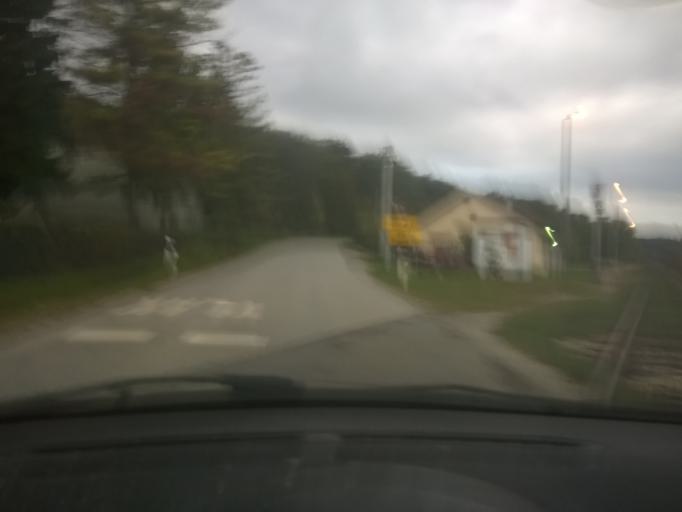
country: HR
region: Zagrebacka
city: Jakovlje
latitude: 45.9759
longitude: 15.8451
